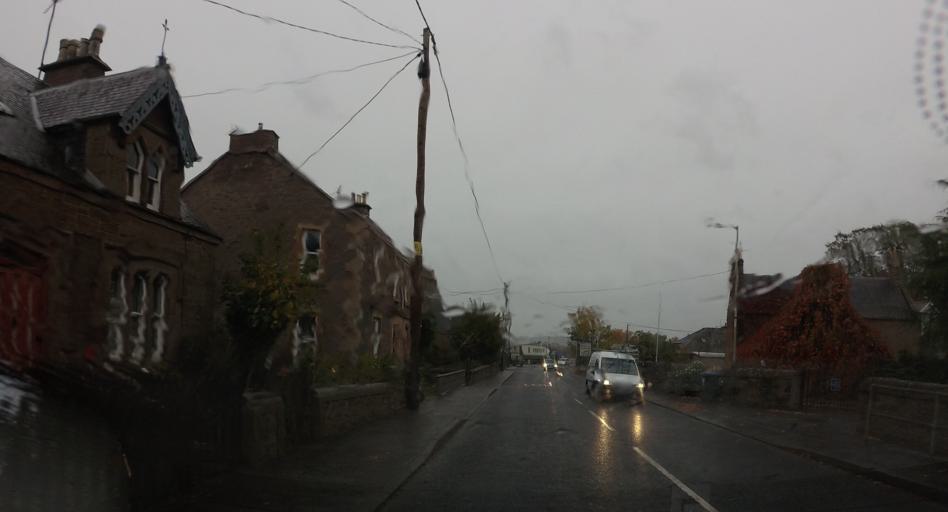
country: GB
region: Scotland
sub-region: Perth and Kinross
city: Coupar Angus
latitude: 56.5483
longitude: -3.2661
